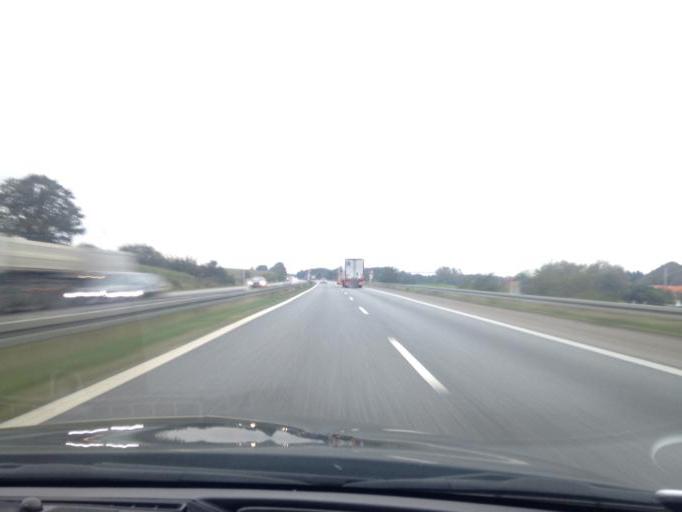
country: DK
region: South Denmark
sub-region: Haderslev Kommune
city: Haderslev
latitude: 55.2676
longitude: 9.4200
